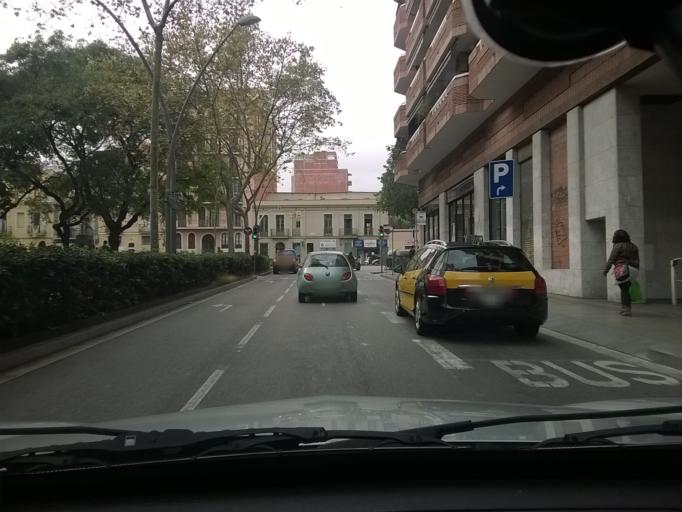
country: ES
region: Catalonia
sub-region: Provincia de Barcelona
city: Gracia
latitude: 41.4042
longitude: 2.1636
